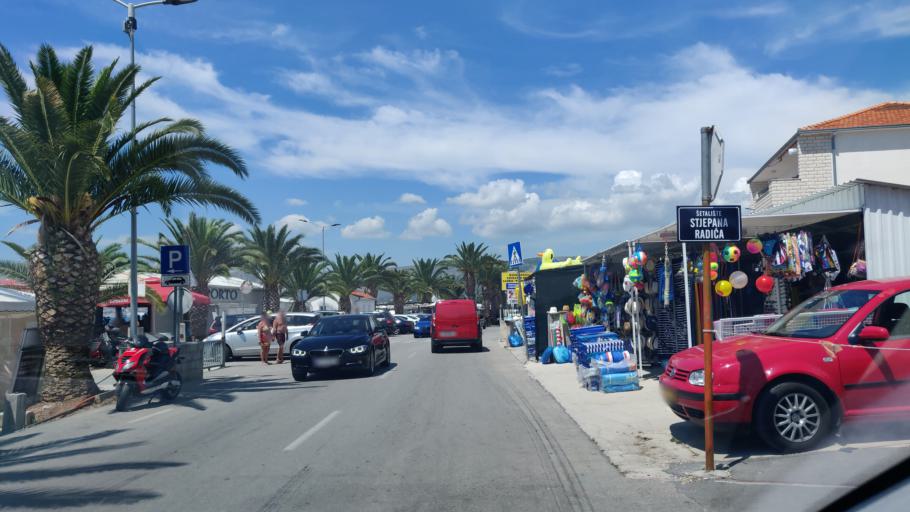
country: HR
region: Splitsko-Dalmatinska
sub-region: Grad Trogir
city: Trogir
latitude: 43.4964
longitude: 16.2608
